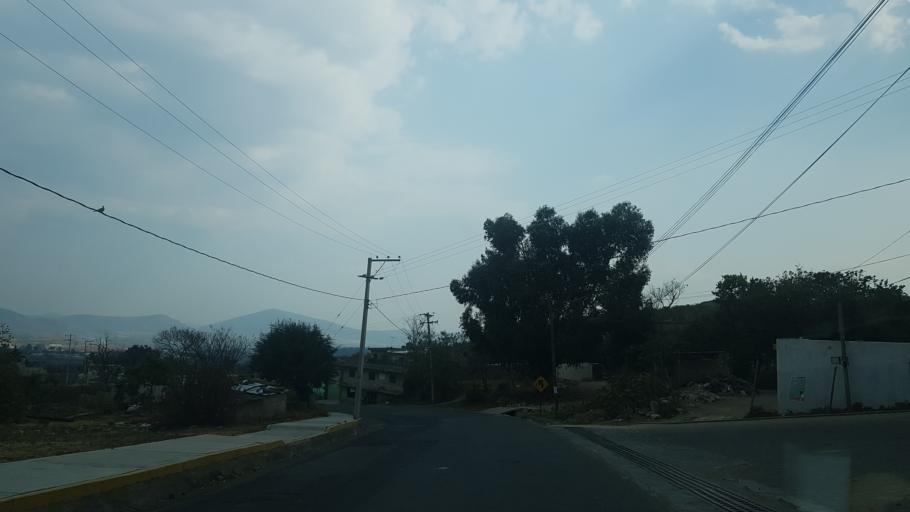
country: MX
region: Puebla
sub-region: Santa Isabel Cholula
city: San Martin Tlamapa
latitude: 18.9768
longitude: -98.3957
